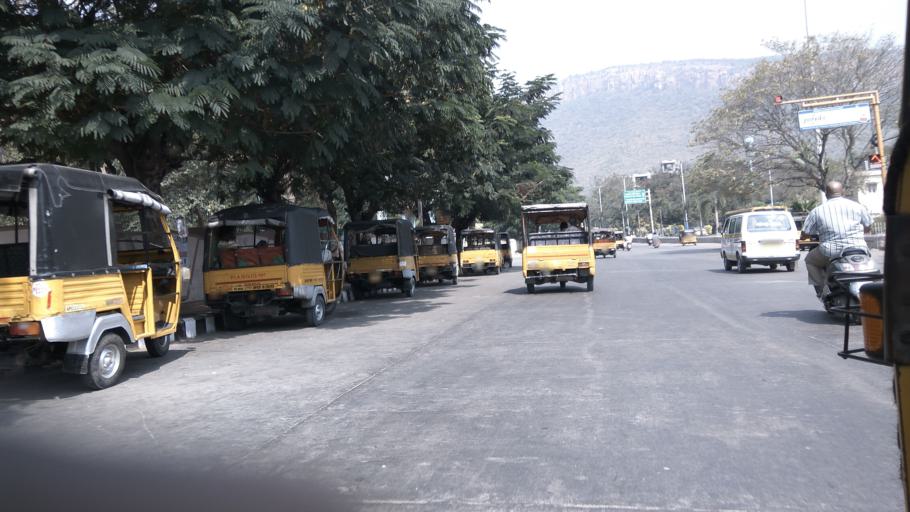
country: IN
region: Andhra Pradesh
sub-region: Chittoor
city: Tirupati
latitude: 13.6421
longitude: 79.4092
